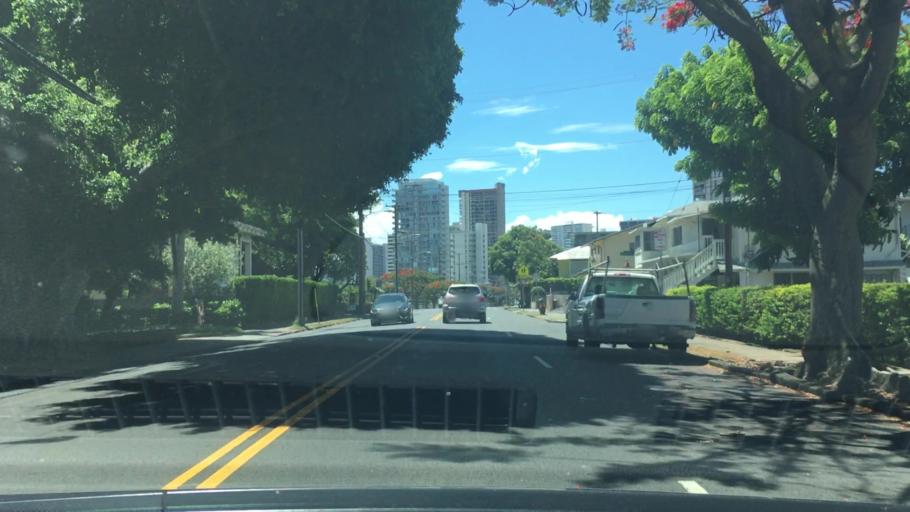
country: US
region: Hawaii
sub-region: Honolulu County
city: Honolulu
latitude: 21.3035
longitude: -157.8338
